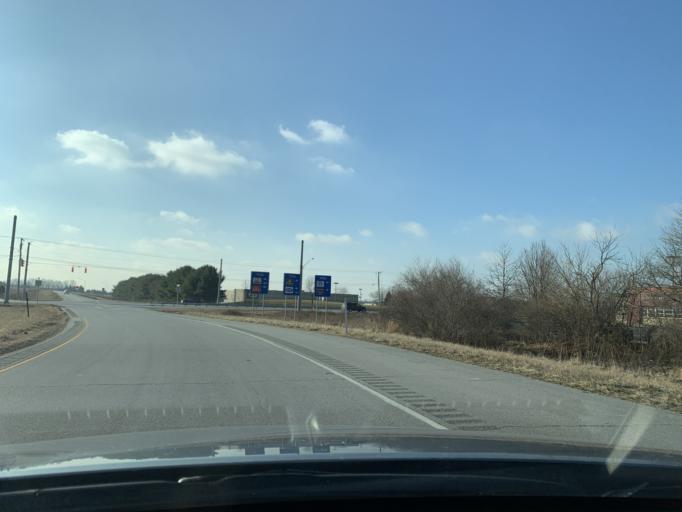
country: US
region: Indiana
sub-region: Porter County
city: Valparaiso
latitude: 41.4705
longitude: -87.0232
